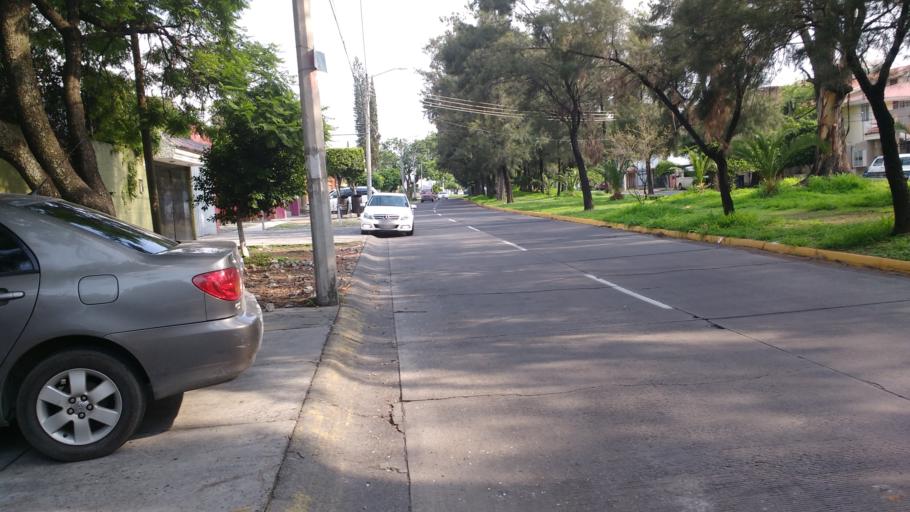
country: MX
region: Jalisco
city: Guadalajara
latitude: 20.6495
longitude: -103.3933
